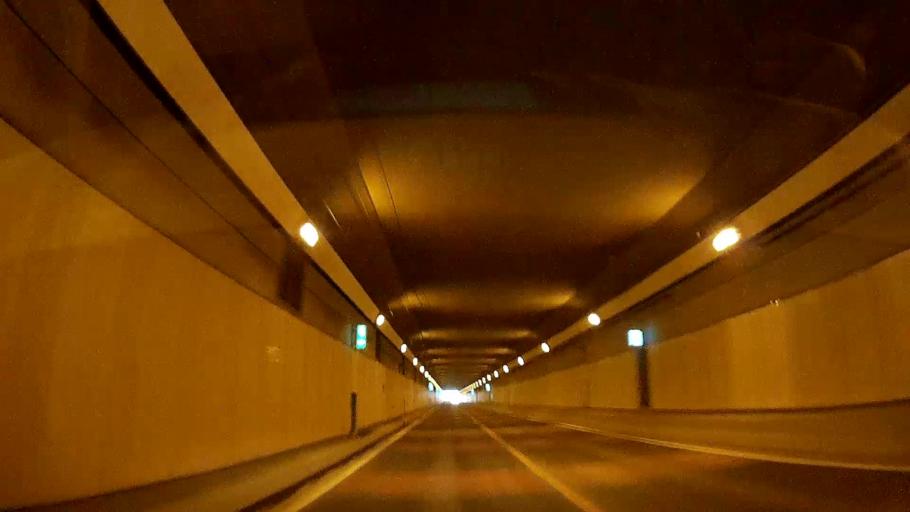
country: JP
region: Kanagawa
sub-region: Kawasaki-shi
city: Kawasaki
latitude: 35.6060
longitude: 139.7911
